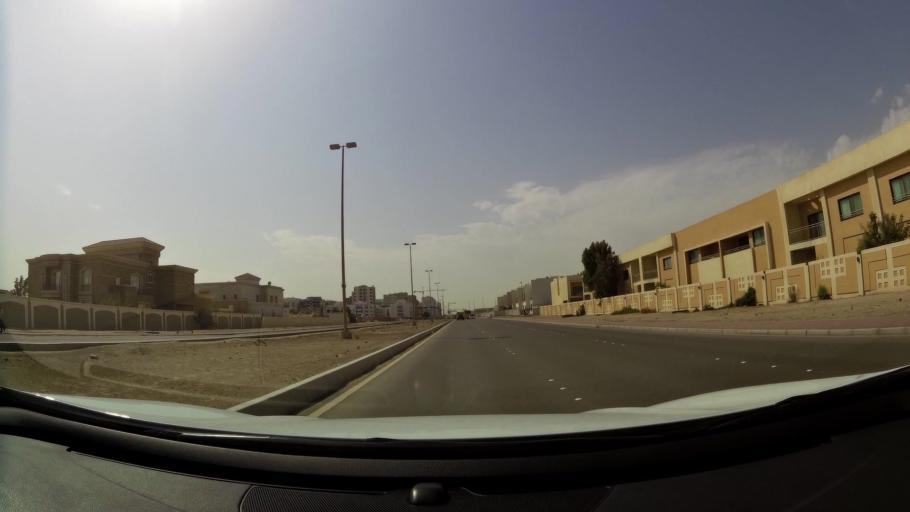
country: AE
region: Abu Dhabi
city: Abu Dhabi
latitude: 24.3384
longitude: 54.5419
